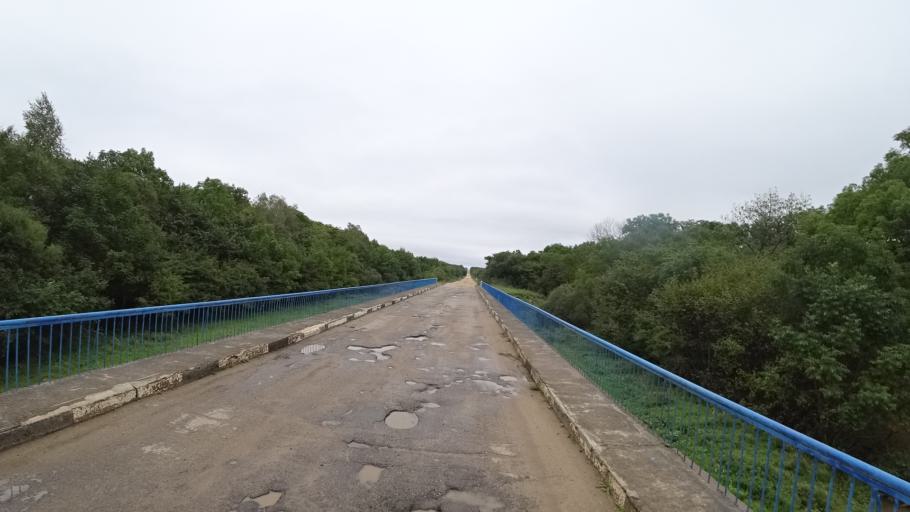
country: RU
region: Primorskiy
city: Ivanovka
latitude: 44.0667
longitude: 132.5746
